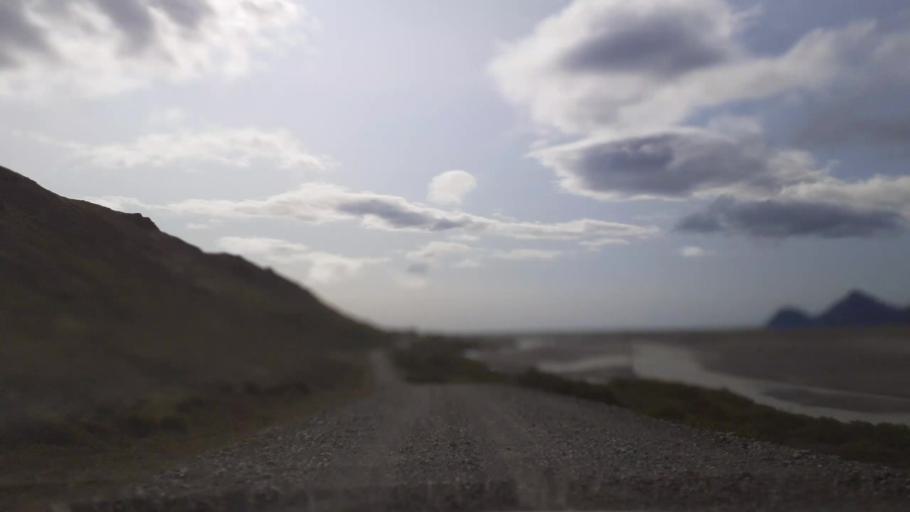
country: IS
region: East
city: Hoefn
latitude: 64.4292
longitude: -14.8862
